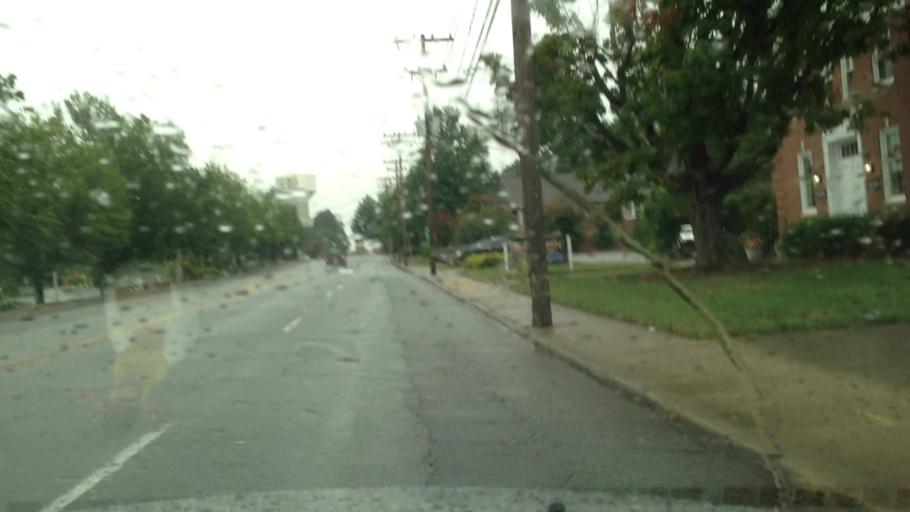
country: US
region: North Carolina
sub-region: Guilford County
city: Greensboro
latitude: 36.0684
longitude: -79.8152
